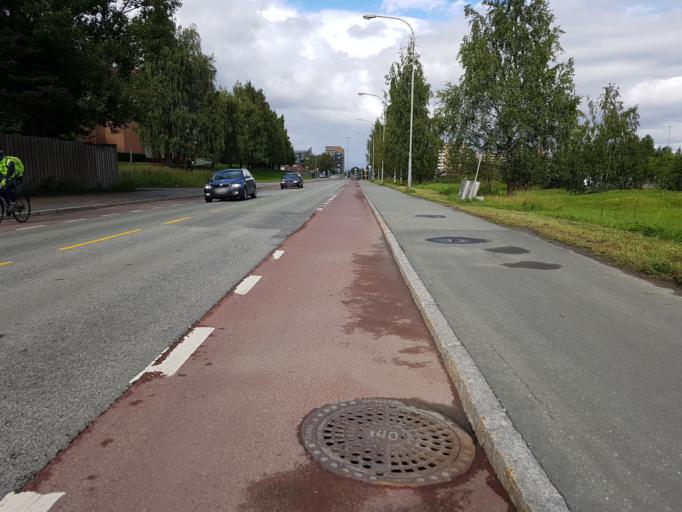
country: NO
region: Sor-Trondelag
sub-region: Trondheim
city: Trondheim
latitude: 63.4183
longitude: 10.4351
